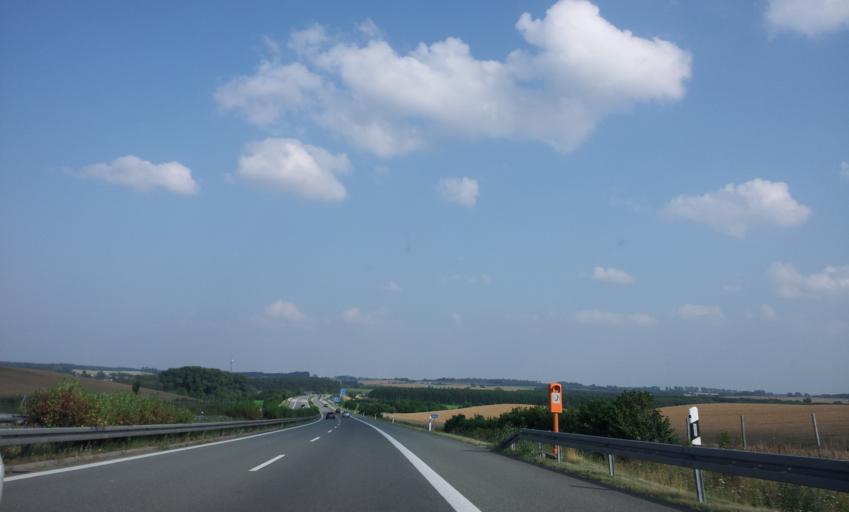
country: DE
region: Mecklenburg-Vorpommern
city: Neuenkirchen
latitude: 53.5922
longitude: 13.3941
